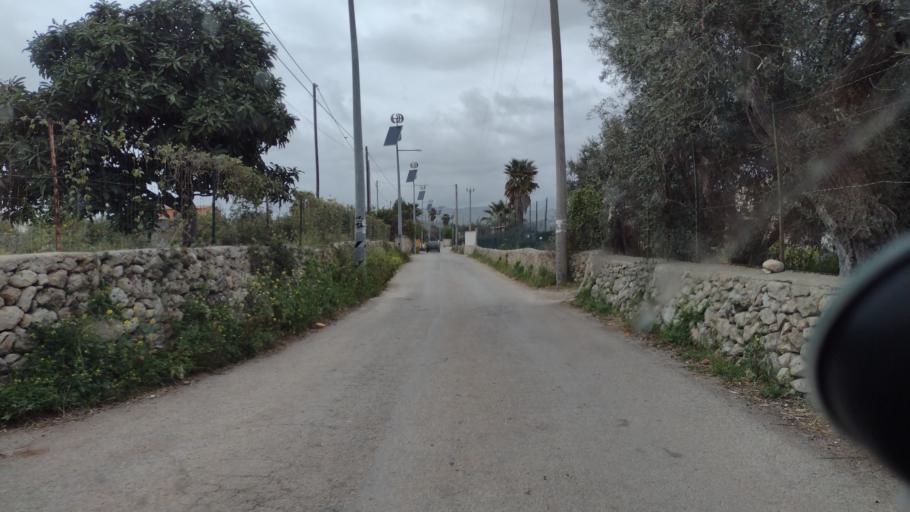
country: IT
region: Sicily
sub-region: Provincia di Siracusa
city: Avola
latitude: 36.8922
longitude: 15.1172
